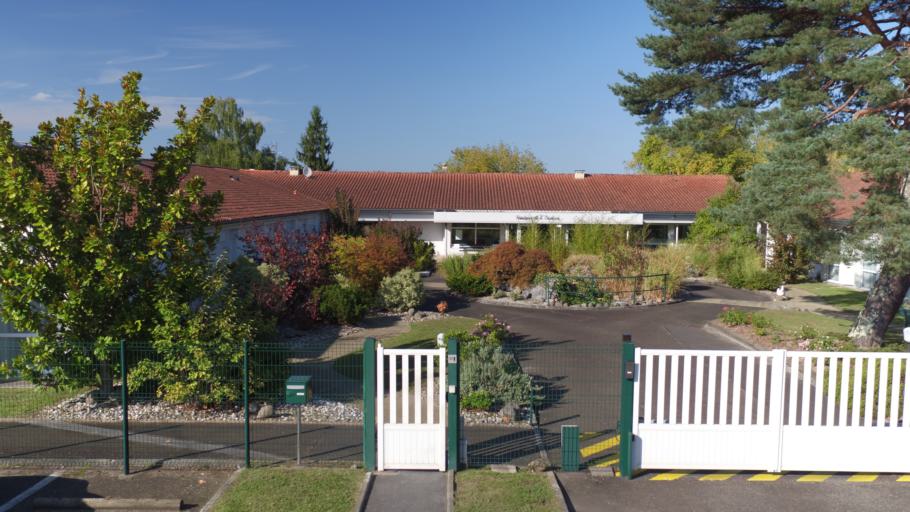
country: FR
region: Aquitaine
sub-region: Departement des Landes
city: Saint-Paul-les-Dax
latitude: 43.7320
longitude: -1.0539
